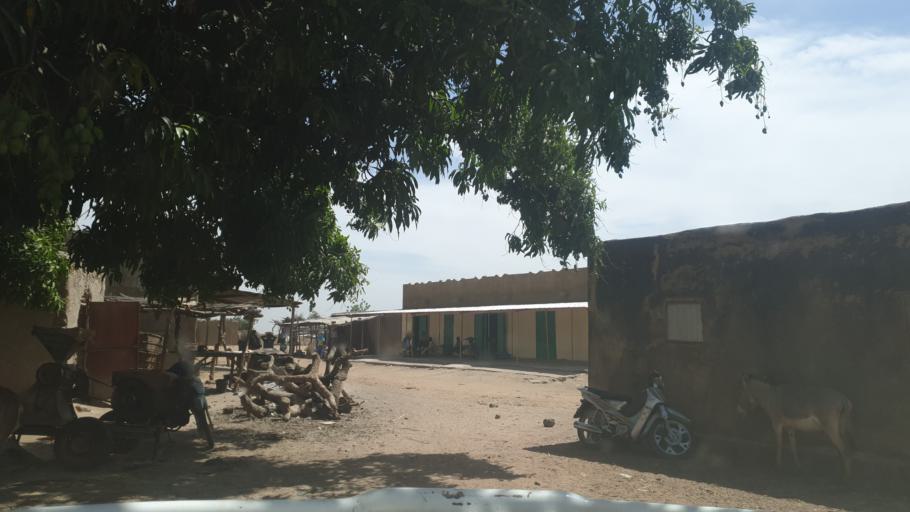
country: ML
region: Sikasso
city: Yorosso
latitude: 12.2915
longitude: -4.6493
